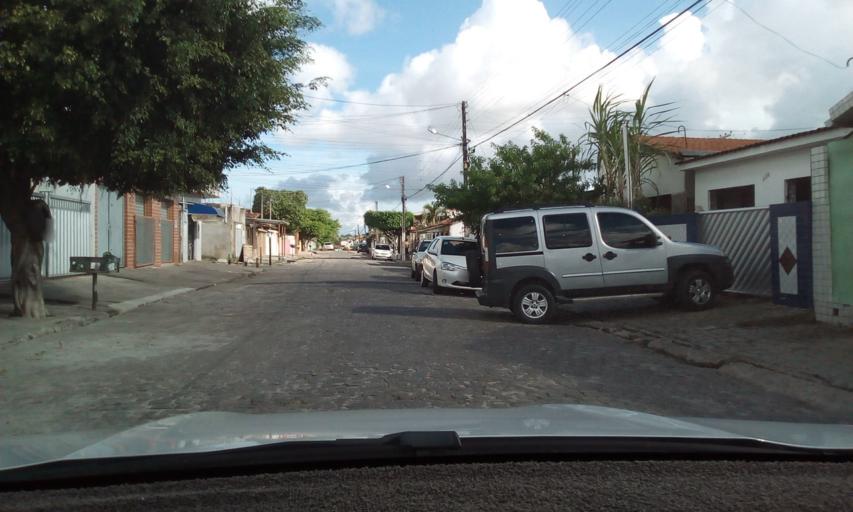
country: BR
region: Paraiba
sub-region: Bayeux
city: Bayeux
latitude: -7.1263
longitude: -34.9219
